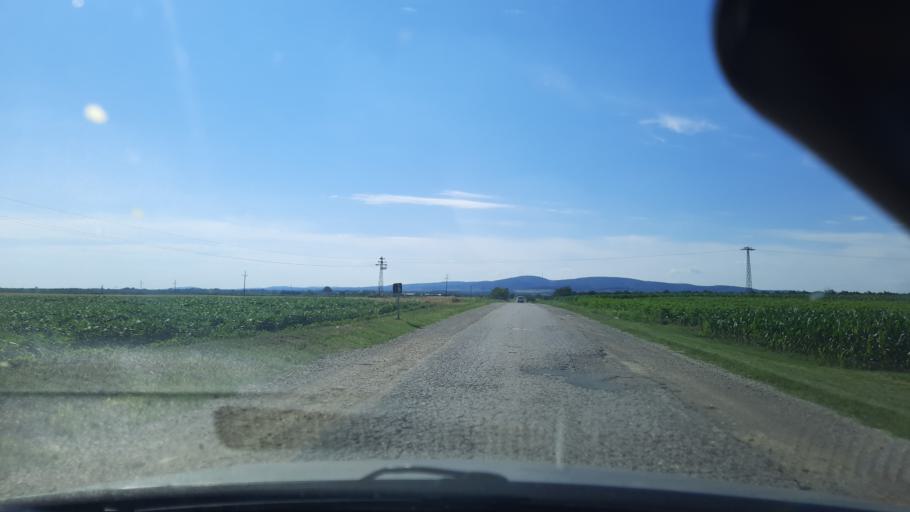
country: RS
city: Cortanovci
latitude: 45.1099
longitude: 19.9743
